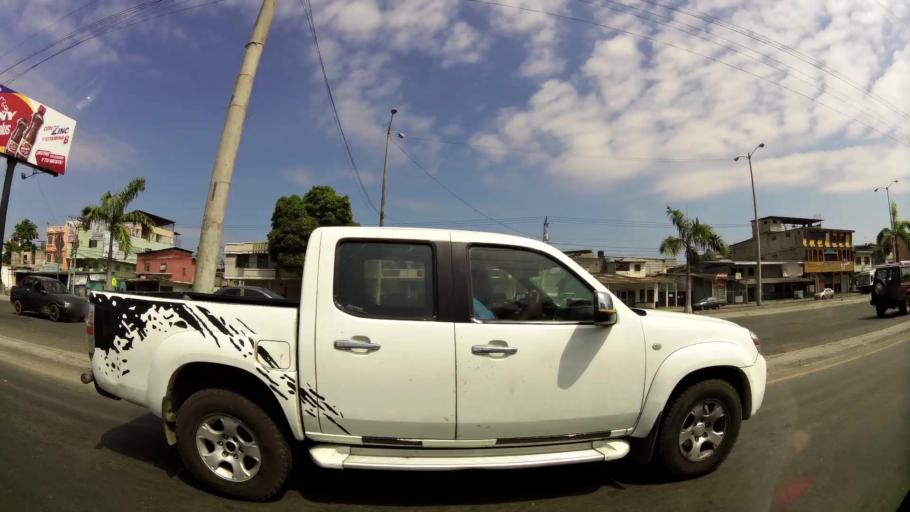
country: EC
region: Guayas
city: Guayaquil
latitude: -2.2526
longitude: -79.8941
